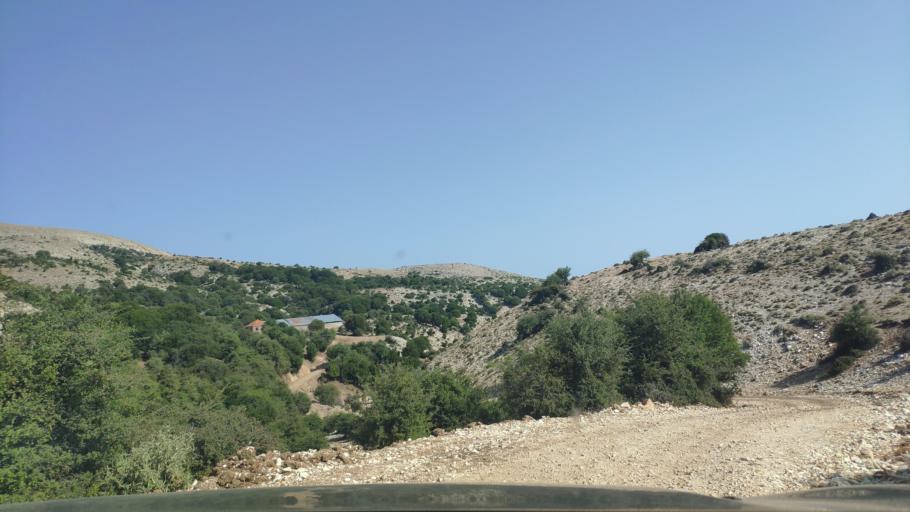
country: GR
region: West Greece
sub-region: Nomos Aitolias kai Akarnanias
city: Monastirakion
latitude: 38.7999
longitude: 20.9971
